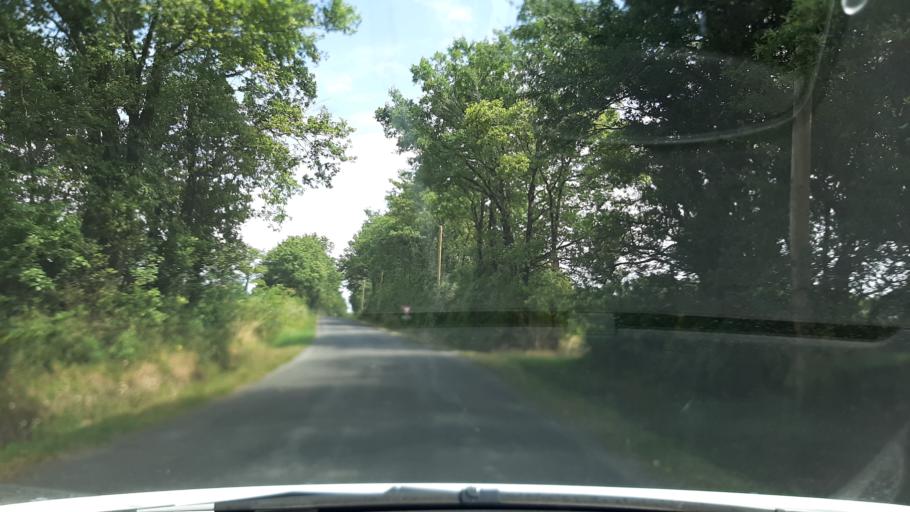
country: FR
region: Pays de la Loire
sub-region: Departement de la Vendee
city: Saint-Etienne-du-Bois
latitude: 46.7875
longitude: -1.5659
